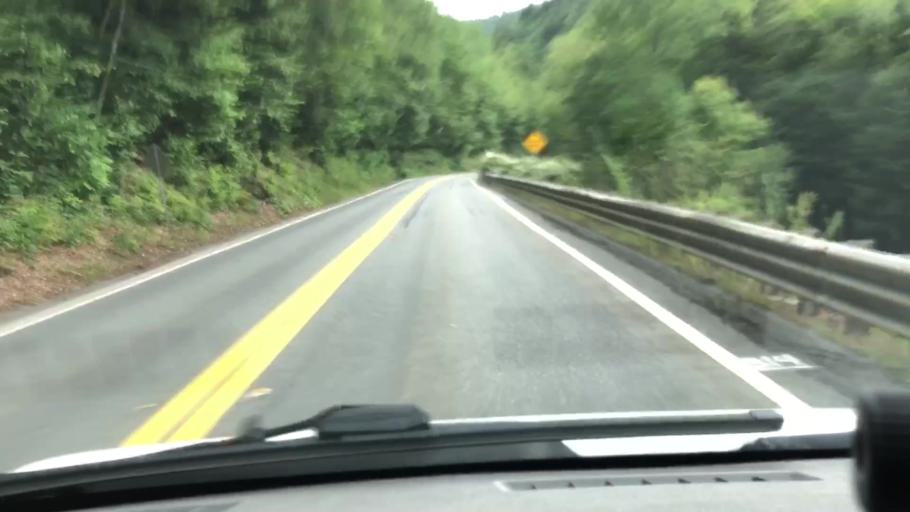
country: US
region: Massachusetts
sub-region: Franklin County
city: Charlemont
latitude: 42.6427
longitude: -72.9902
